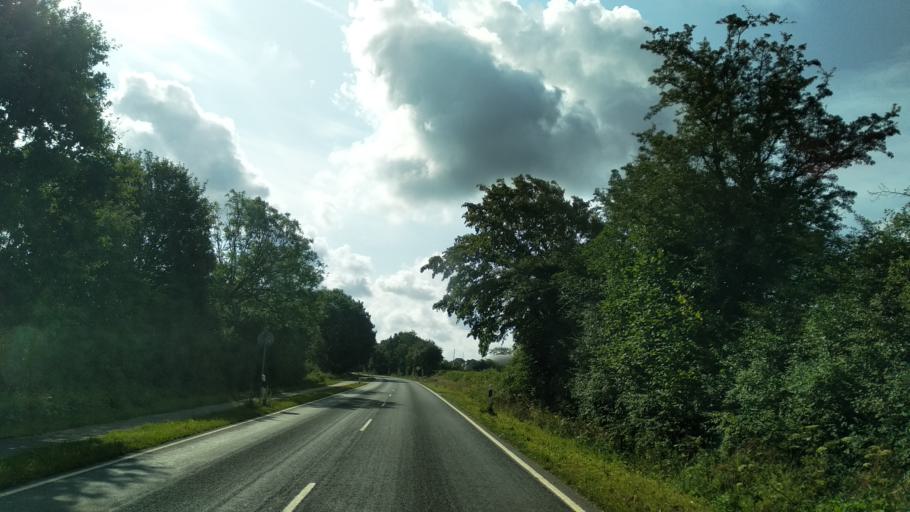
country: DE
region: Schleswig-Holstein
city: Busdorf
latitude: 54.4880
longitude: 9.5574
